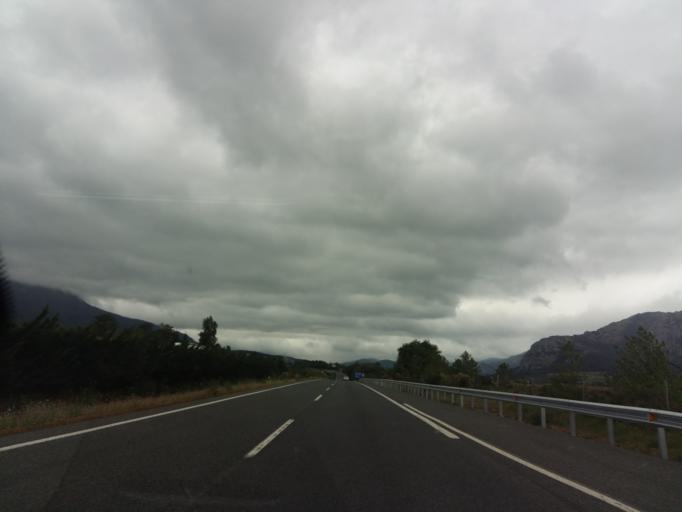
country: ES
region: Navarre
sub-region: Provincia de Navarra
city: Iraneta
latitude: 42.9166
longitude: -1.9281
